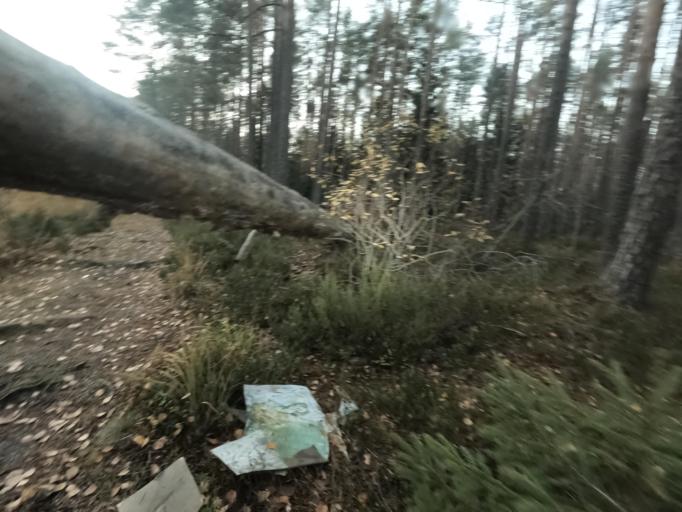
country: RU
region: St.-Petersburg
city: Komarovo
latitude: 60.2024
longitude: 29.8057
